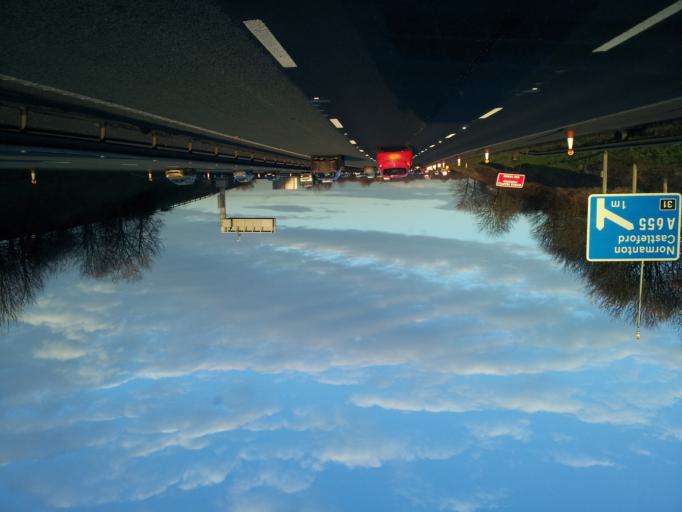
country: GB
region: England
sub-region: City and Borough of Wakefield
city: Castleford
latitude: 53.7061
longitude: -1.3642
